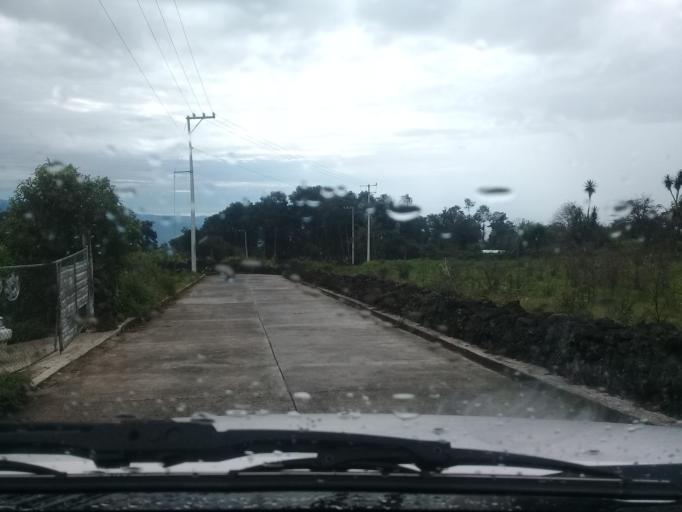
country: MX
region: Veracruz
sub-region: Acajete
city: La Joya
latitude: 19.6163
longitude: -97.0028
